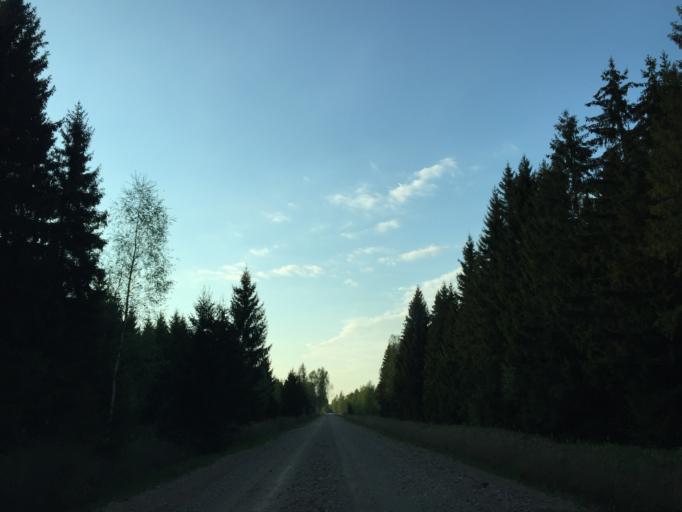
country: LV
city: Tireli
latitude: 56.8488
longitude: 23.6951
